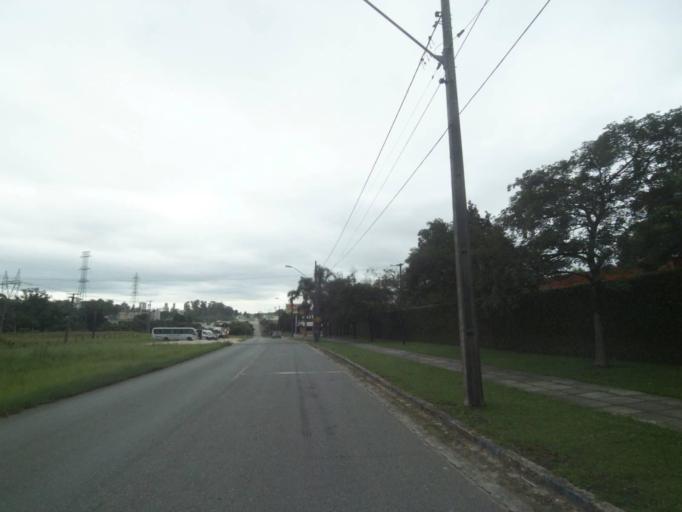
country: BR
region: Parana
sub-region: Sao Jose Dos Pinhais
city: Sao Jose dos Pinhais
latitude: -25.5438
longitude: -49.3103
